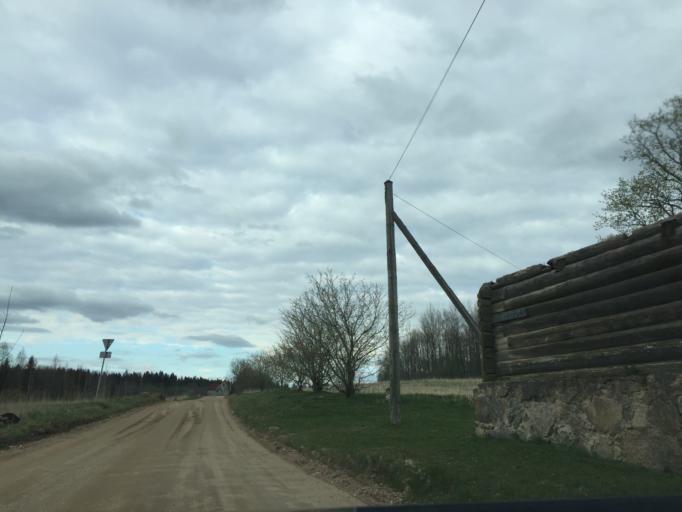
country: LV
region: Aluksnes Rajons
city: Aluksne
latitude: 57.4154
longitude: 27.0141
